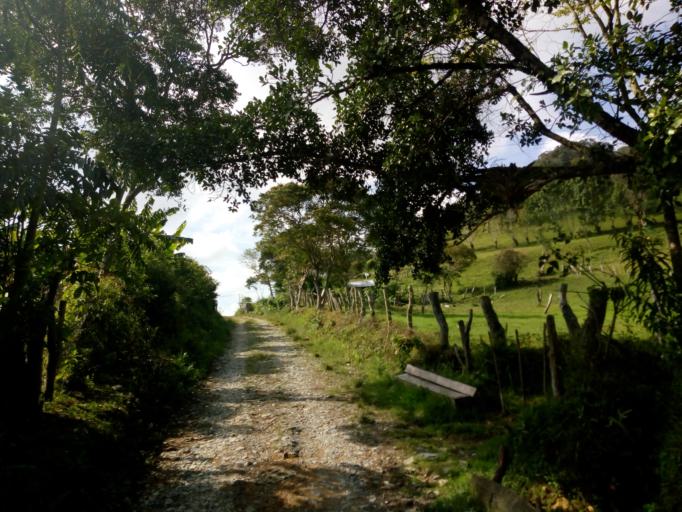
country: CO
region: Boyaca
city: Moniquira
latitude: 5.8743
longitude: -73.5046
